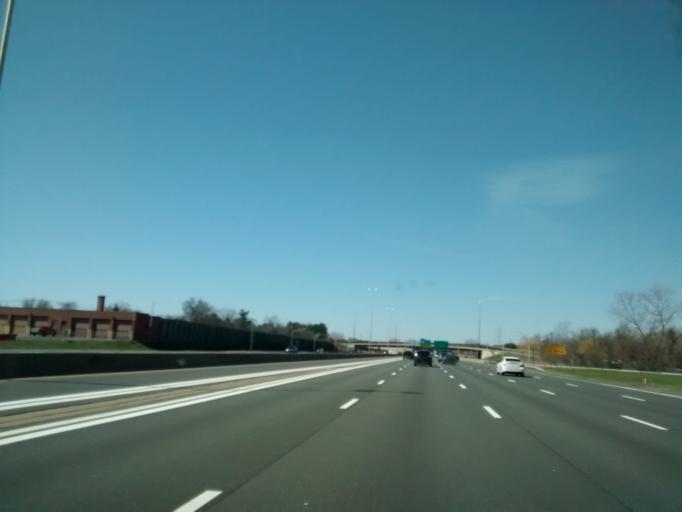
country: US
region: Connecticut
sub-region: Hartford County
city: East Hartford
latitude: 41.7672
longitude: -72.6202
